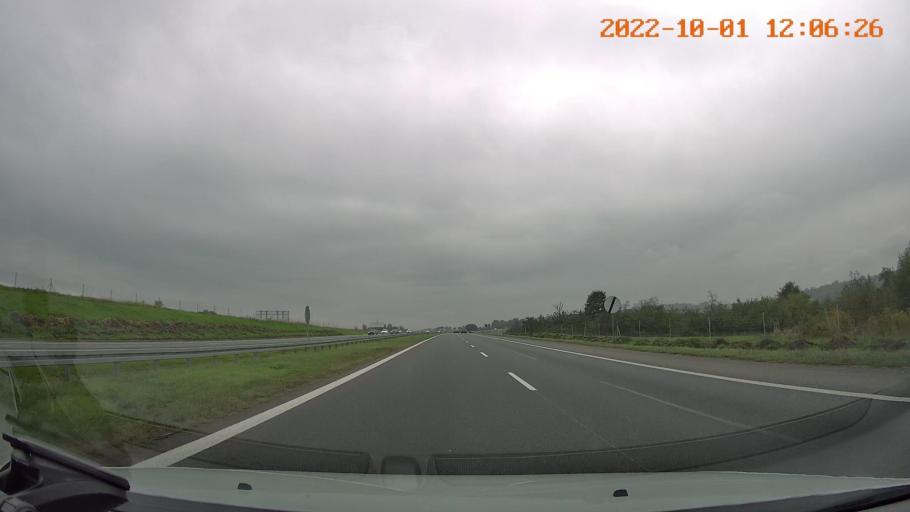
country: PL
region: Lesser Poland Voivodeship
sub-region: Powiat krakowski
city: Mnikow
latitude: 50.0780
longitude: 19.7405
